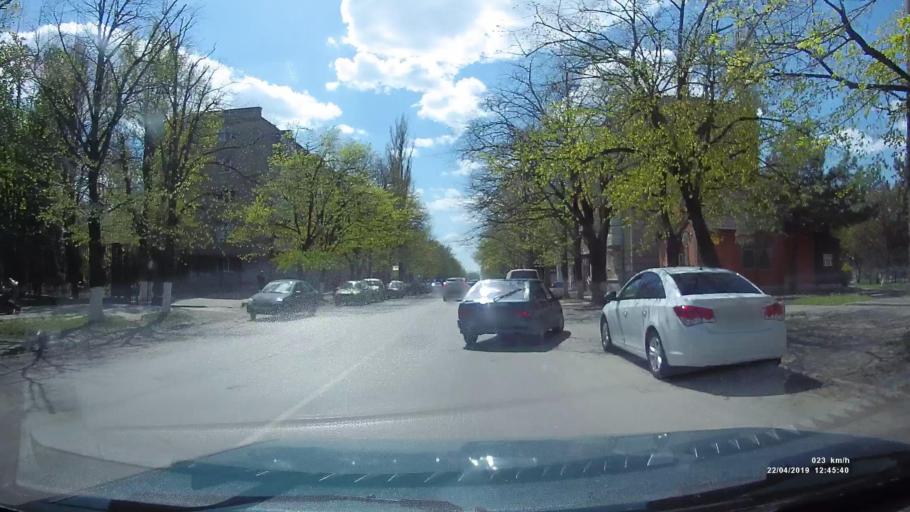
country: RU
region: Rostov
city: Azov
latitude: 47.1029
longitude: 39.4137
